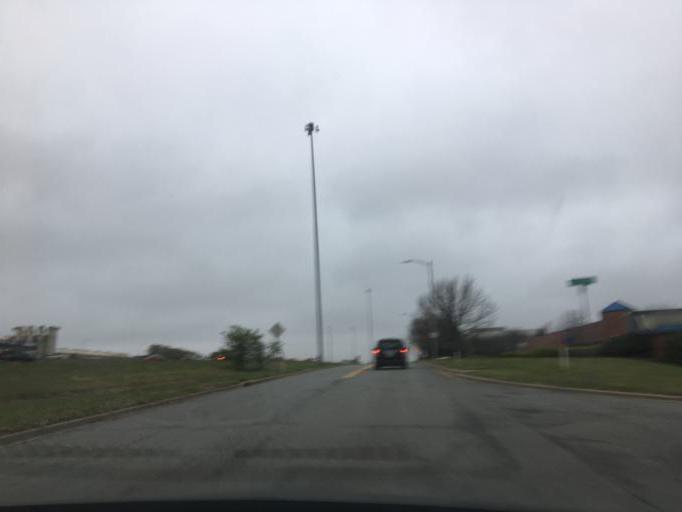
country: US
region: Kansas
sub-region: Johnson County
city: Overland Park
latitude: 38.9844
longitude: -94.7069
